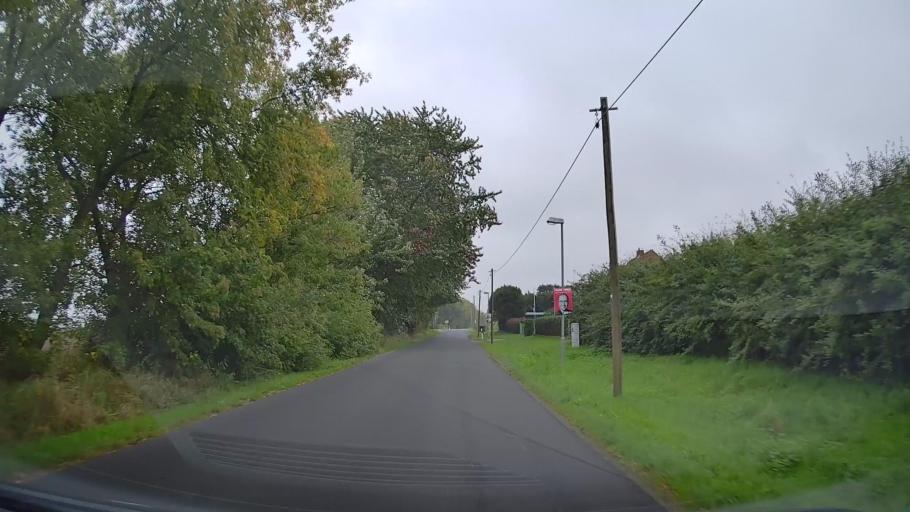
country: DE
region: Mecklenburg-Vorpommern
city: Hornstorf
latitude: 53.9245
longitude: 11.5413
